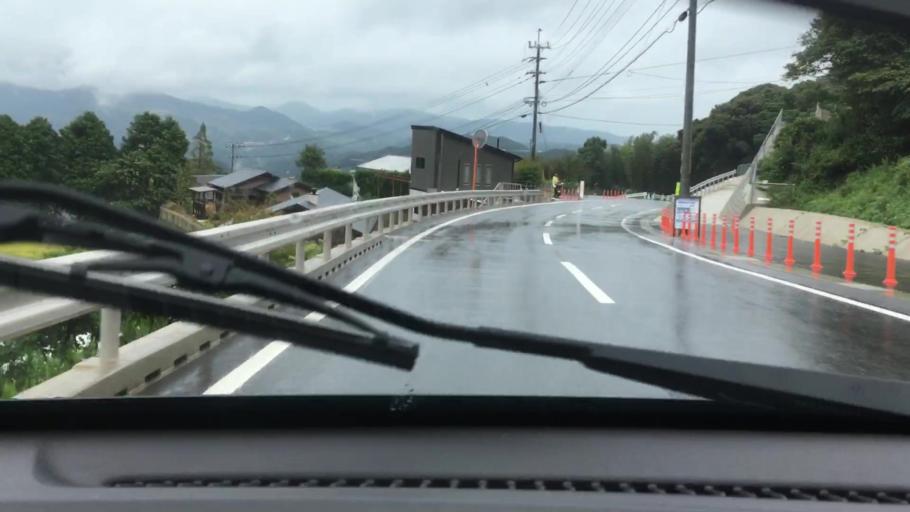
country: JP
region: Nagasaki
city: Togitsu
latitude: 32.8691
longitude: 129.7667
